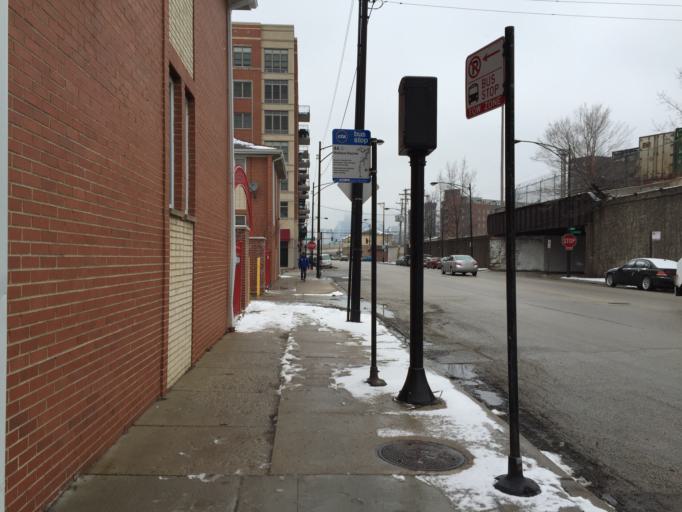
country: US
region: Illinois
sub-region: Cook County
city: Chicago
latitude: 41.8495
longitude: -87.6386
